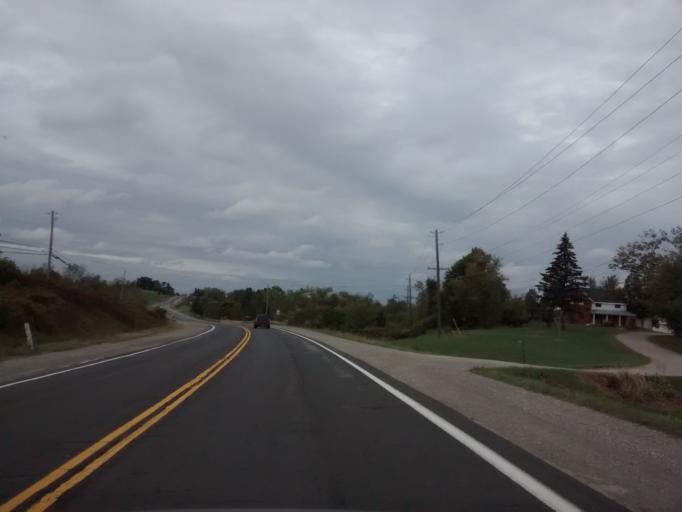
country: CA
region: Ontario
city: Ancaster
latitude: 43.0459
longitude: -79.9768
